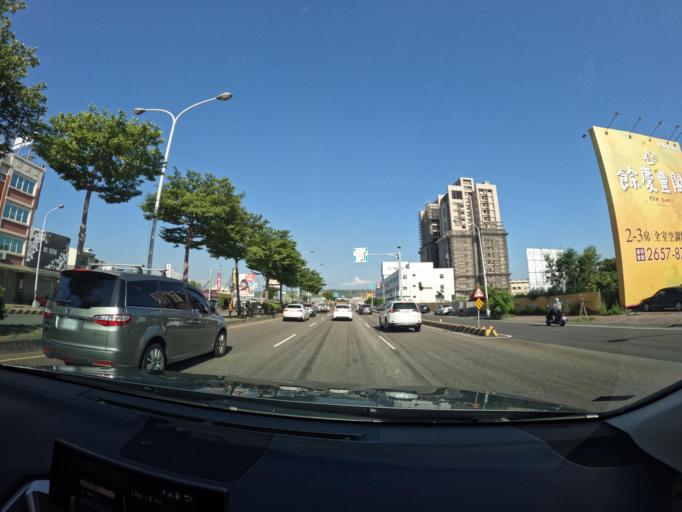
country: TW
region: Taiwan
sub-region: Taichung City
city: Taichung
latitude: 24.2451
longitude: 120.5491
